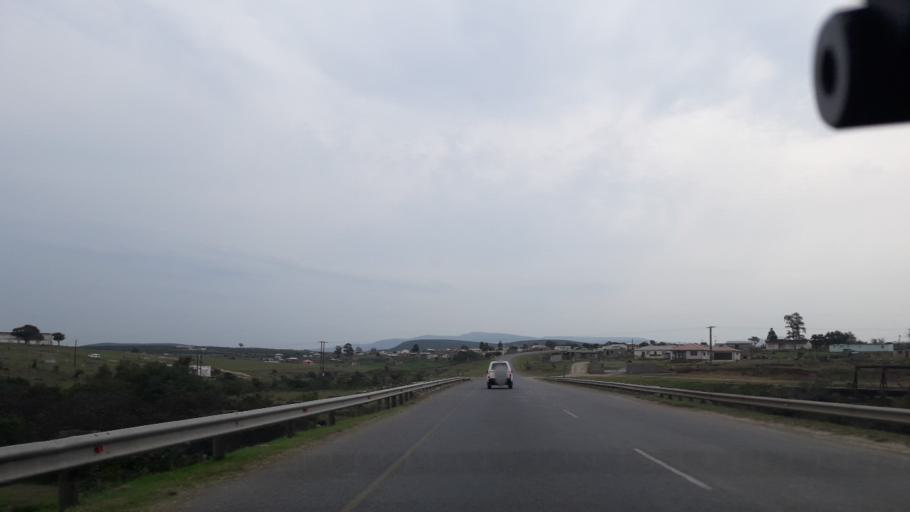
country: ZA
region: Eastern Cape
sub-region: Buffalo City Metropolitan Municipality
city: Bhisho
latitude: -32.8316
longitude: 27.3795
